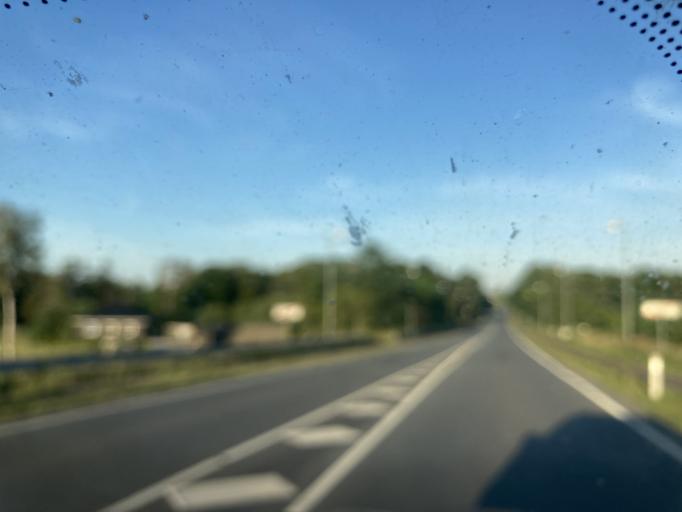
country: DK
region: Zealand
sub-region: Lejre Kommune
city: Lejre
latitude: 55.6405
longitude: 11.9622
